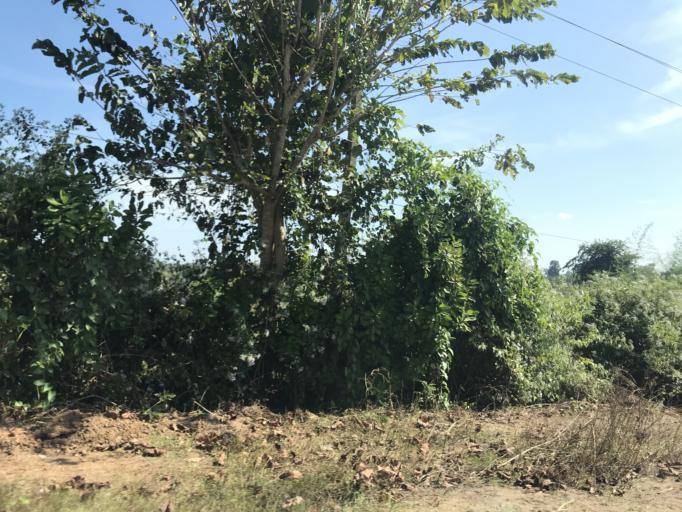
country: IN
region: Karnataka
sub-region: Mysore
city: Heggadadevankote
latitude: 11.9668
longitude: 76.2555
